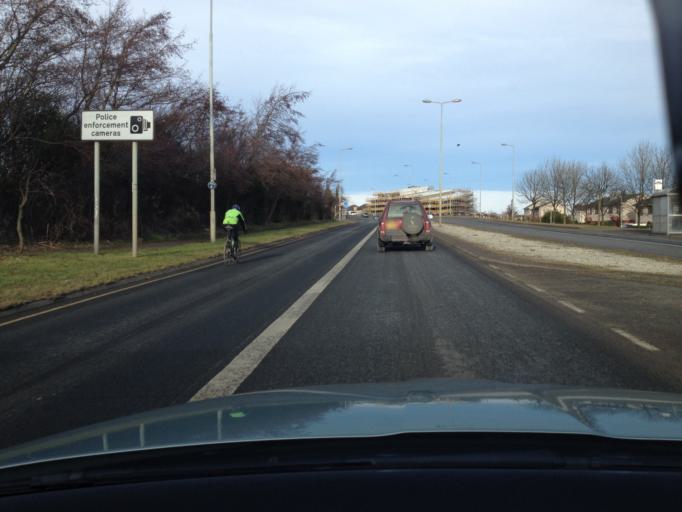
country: GB
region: Scotland
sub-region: Midlothian
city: Loanhead
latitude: 55.8963
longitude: -3.1615
